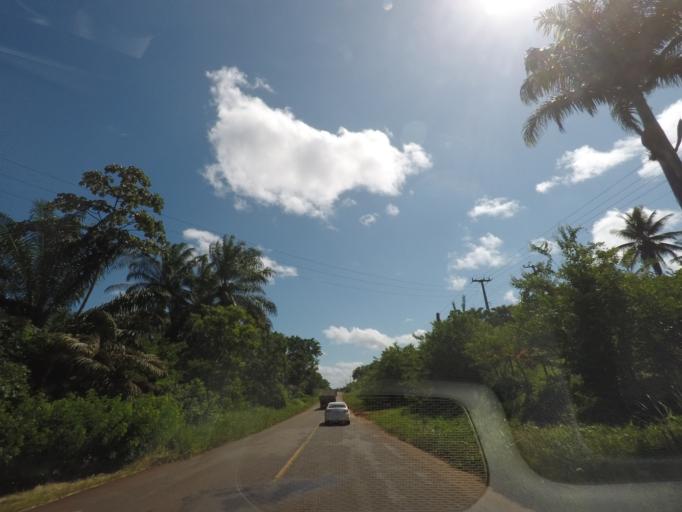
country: BR
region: Bahia
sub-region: Itubera
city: Itubera
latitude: -13.6709
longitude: -39.1222
